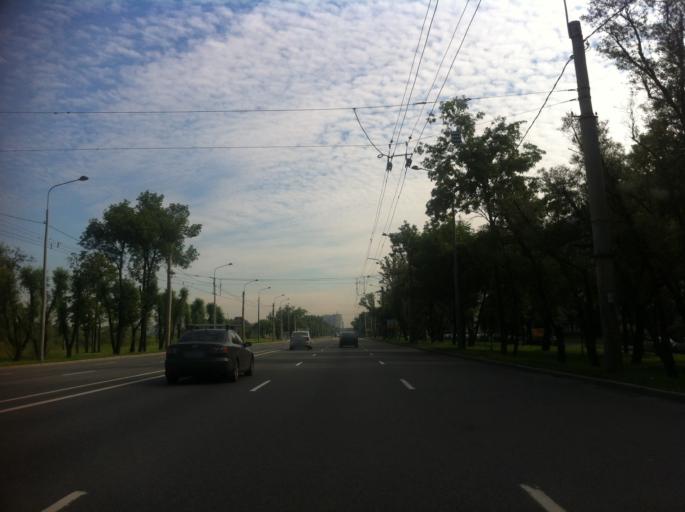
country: RU
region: St.-Petersburg
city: Uritsk
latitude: 59.8346
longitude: 30.1969
